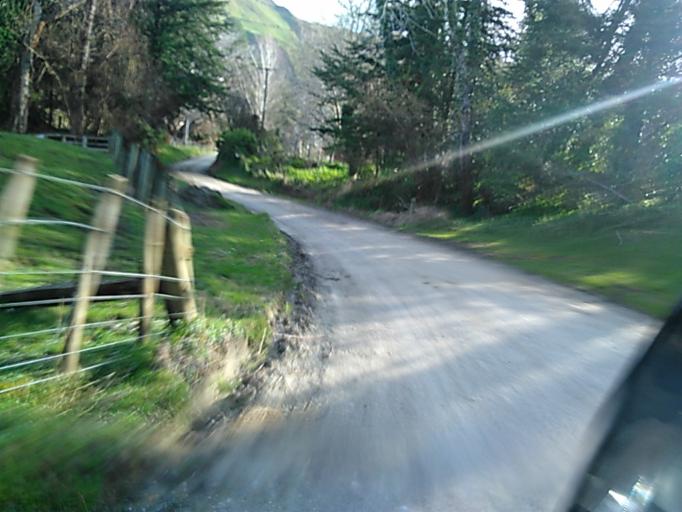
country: NZ
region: Gisborne
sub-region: Gisborne District
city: Gisborne
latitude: -38.5891
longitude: 178.0658
